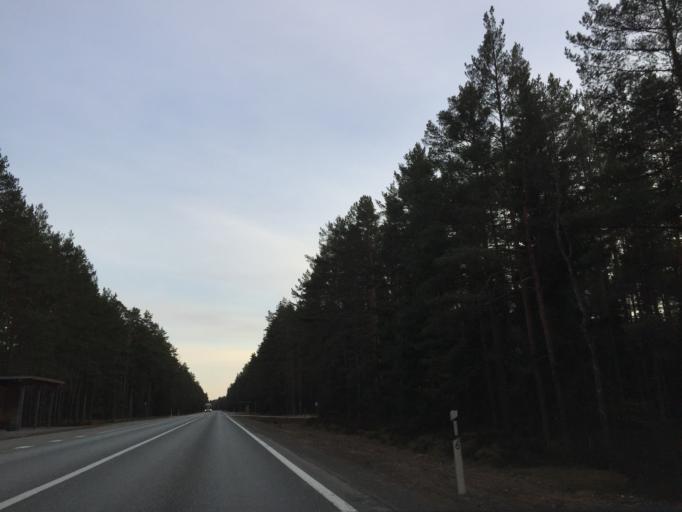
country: LV
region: Salacgrivas
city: Salacgriva
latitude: 57.5406
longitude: 24.4318
